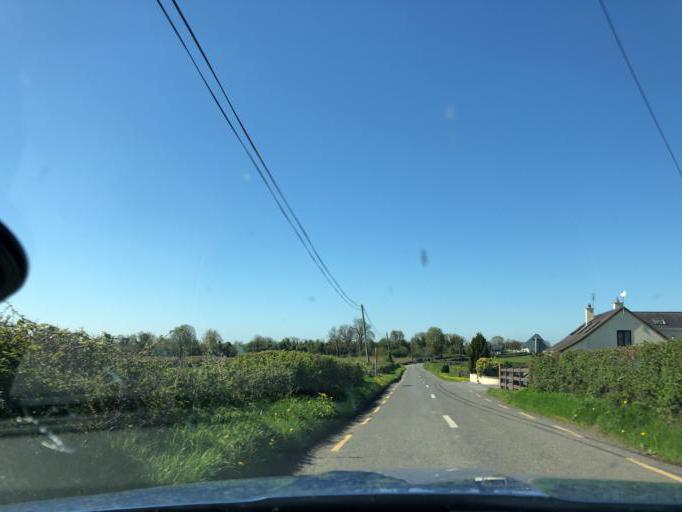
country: IE
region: Connaught
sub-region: County Galway
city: Portumna
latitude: 53.1861
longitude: -8.1663
